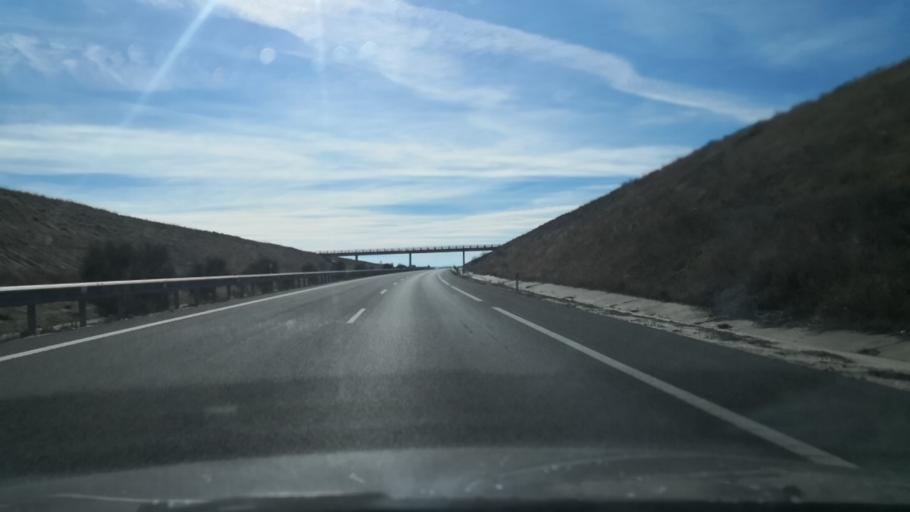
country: ES
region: Castille and Leon
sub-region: Provincia de Avila
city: Crespos
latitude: 40.8671
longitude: -4.9865
